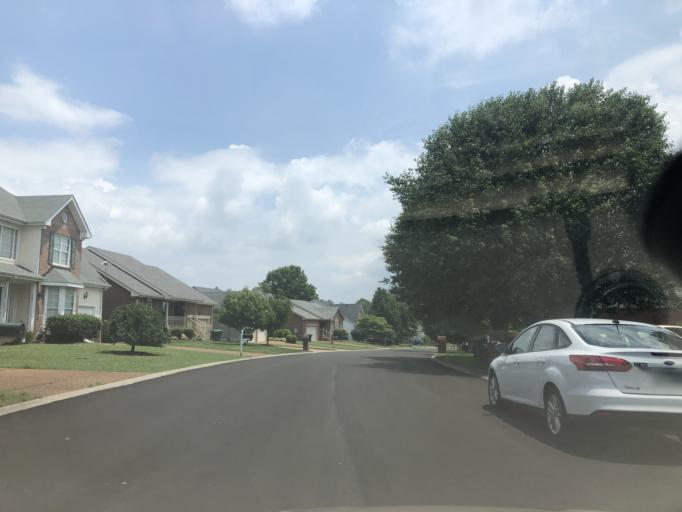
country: US
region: Tennessee
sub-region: Davidson County
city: Lakewood
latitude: 36.2171
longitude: -86.6319
